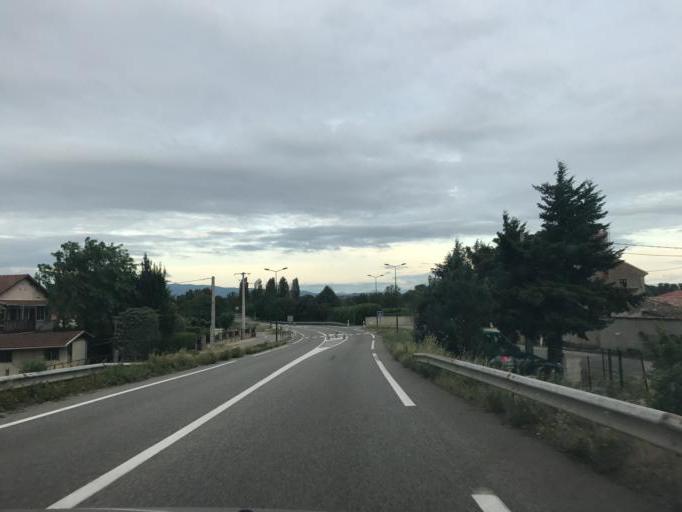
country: FR
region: Rhone-Alpes
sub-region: Departement de l'Ardeche
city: Charmes-sur-Rhone
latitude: 44.8555
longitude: 4.8338
